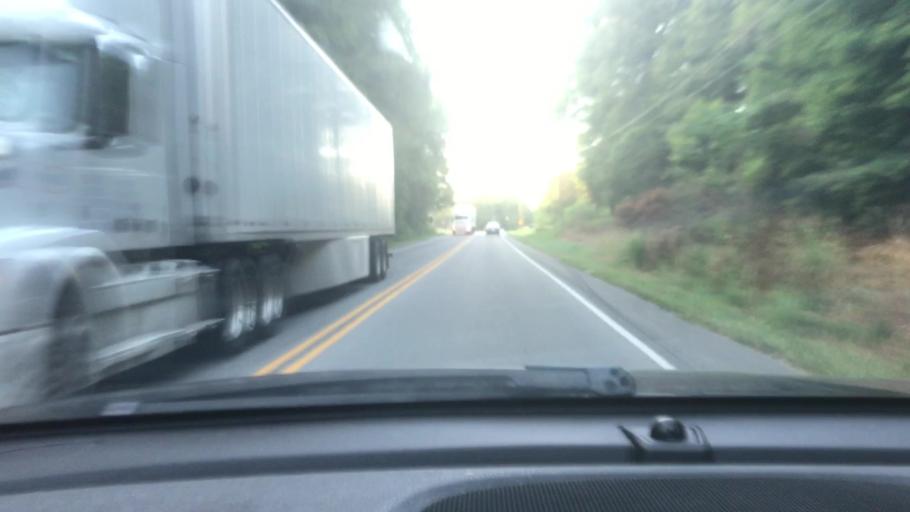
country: US
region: Tennessee
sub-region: Dickson County
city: Dickson
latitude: 36.1027
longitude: -87.3742
